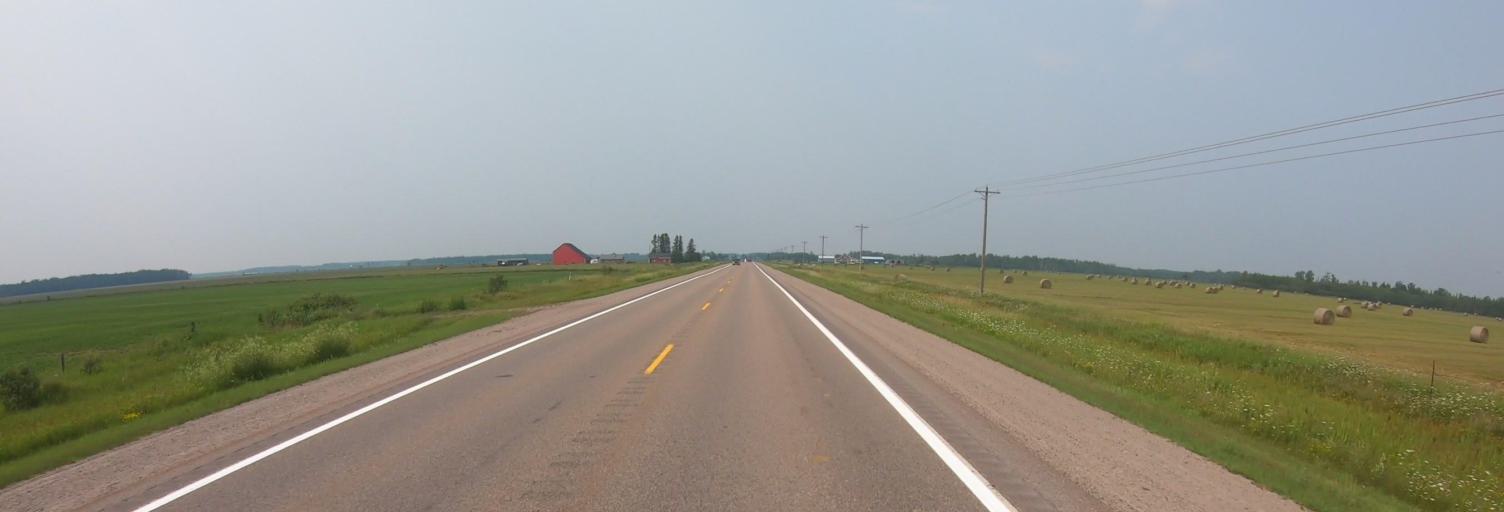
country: US
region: Michigan
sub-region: Chippewa County
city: Sault Ste. Marie
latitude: 46.3521
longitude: -84.3640
